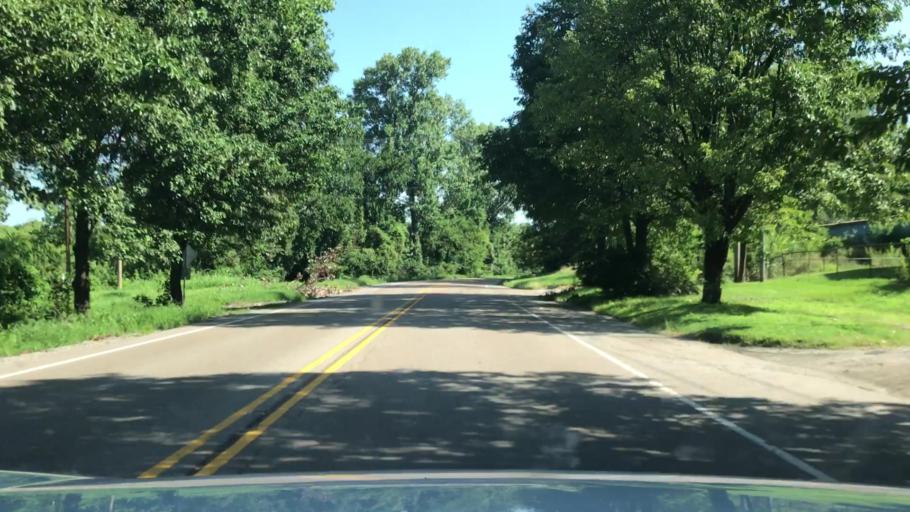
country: US
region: Illinois
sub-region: Madison County
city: Venice
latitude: 38.6585
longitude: -90.1702
